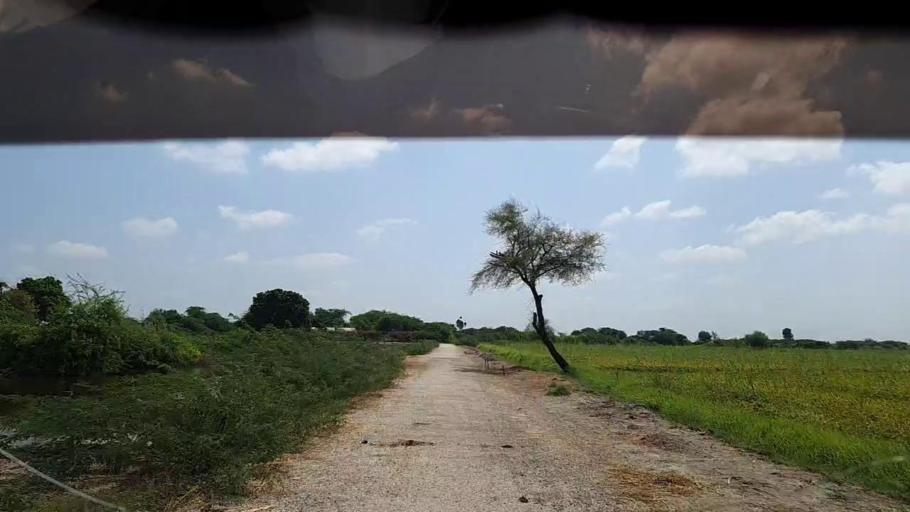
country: PK
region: Sindh
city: Kadhan
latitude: 24.5832
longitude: 68.9607
